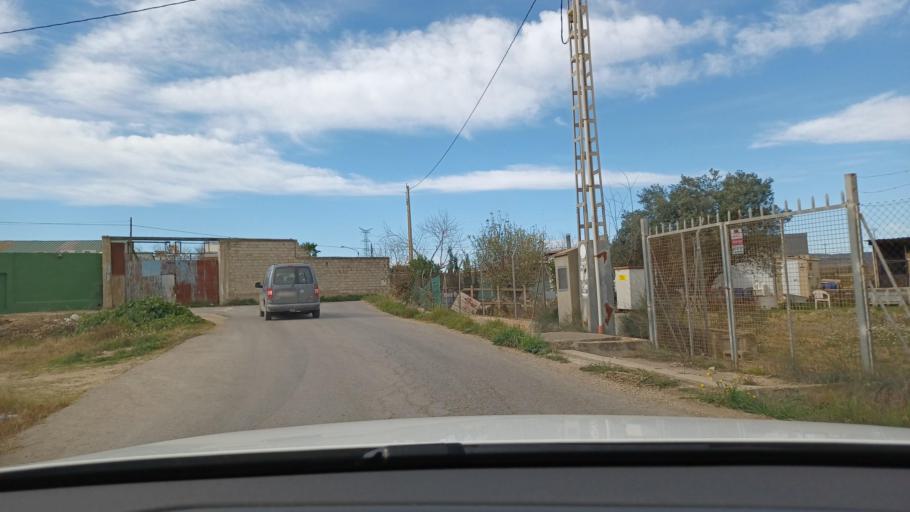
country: ES
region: Valencia
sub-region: Provincia de Valencia
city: Benifaio
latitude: 39.2886
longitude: -0.4329
